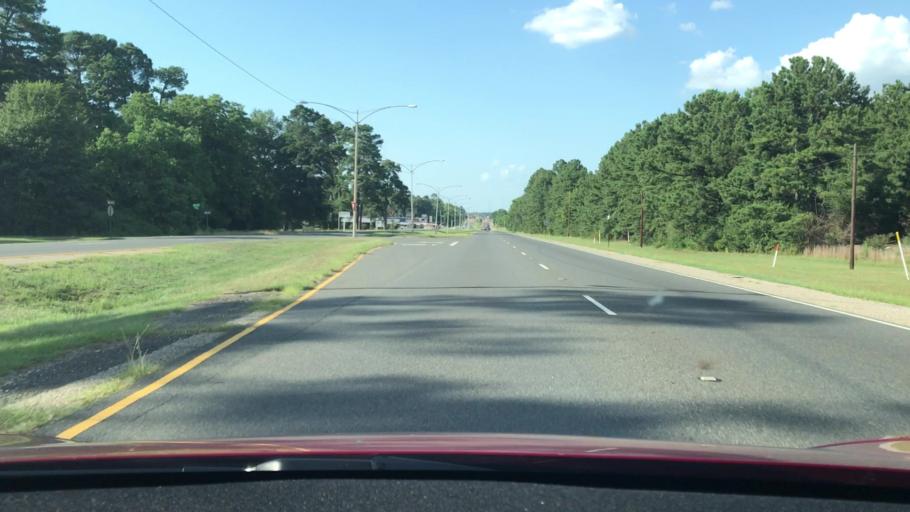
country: US
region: Louisiana
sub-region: Bossier Parish
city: Bossier City
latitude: 32.4213
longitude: -93.7872
